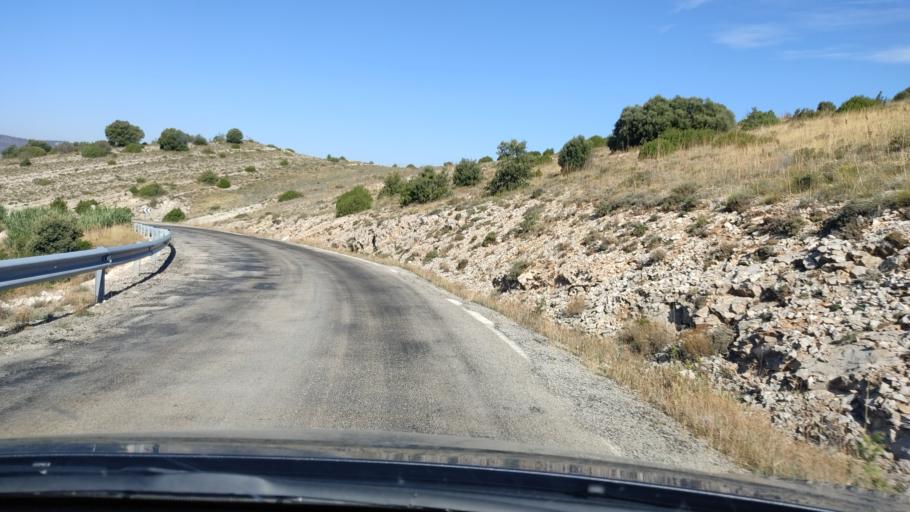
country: ES
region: Aragon
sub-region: Provincia de Teruel
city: Fonfria
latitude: 41.0028
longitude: -1.0610
